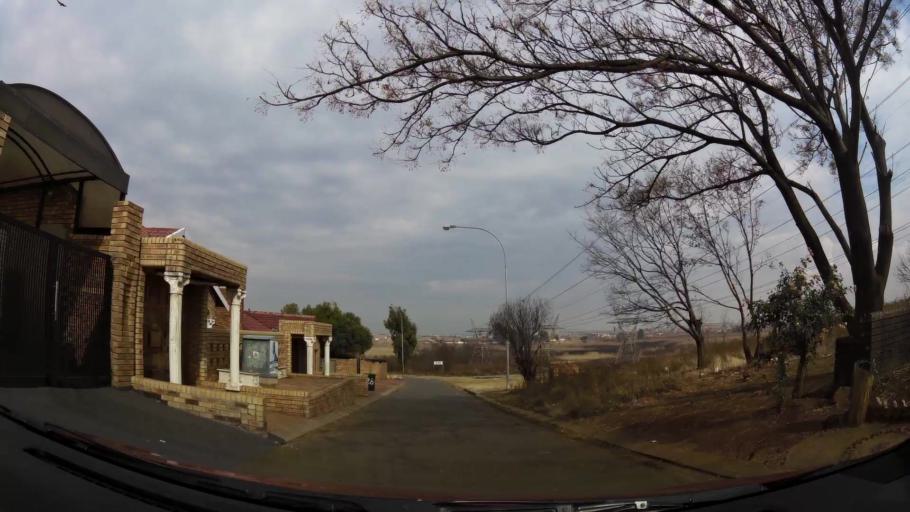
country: ZA
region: Gauteng
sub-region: City of Johannesburg Metropolitan Municipality
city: Soweto
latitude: -26.2670
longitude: 27.8251
